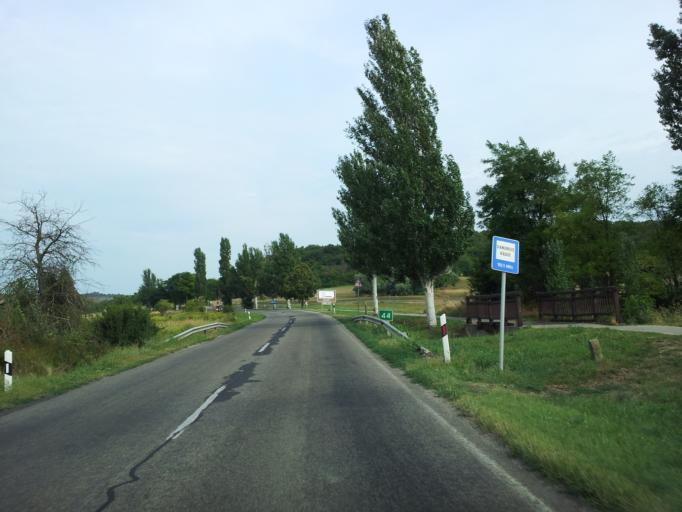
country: HU
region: Veszprem
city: Tihany
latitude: 46.9214
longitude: 17.8500
